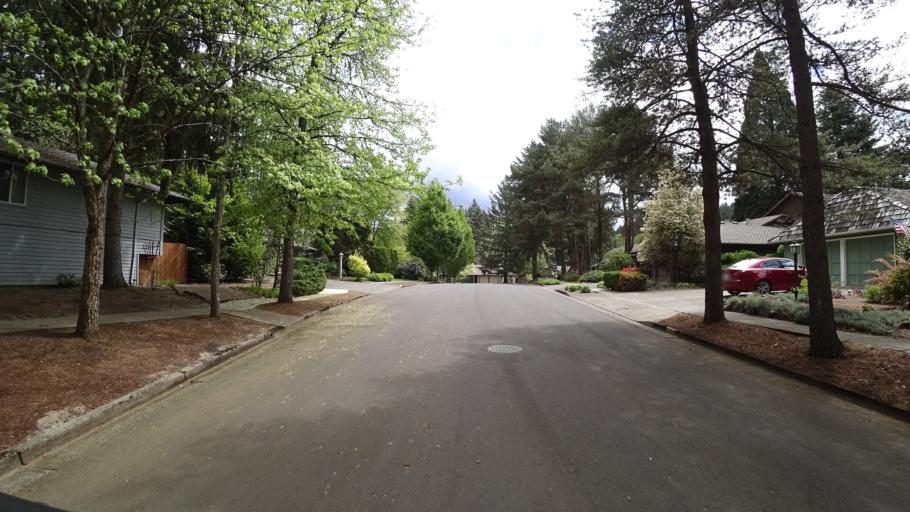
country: US
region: Oregon
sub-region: Washington County
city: Beaverton
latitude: 45.4769
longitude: -122.8358
